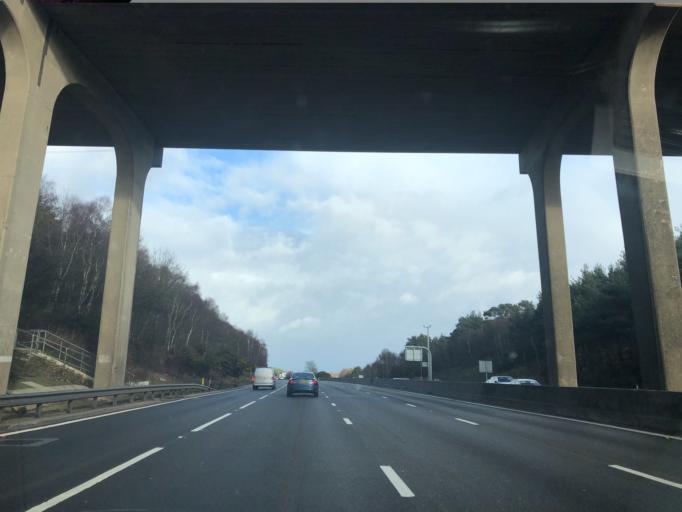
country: GB
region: England
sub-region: Surrey
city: Bagshot
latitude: 51.3373
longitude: -0.7075
